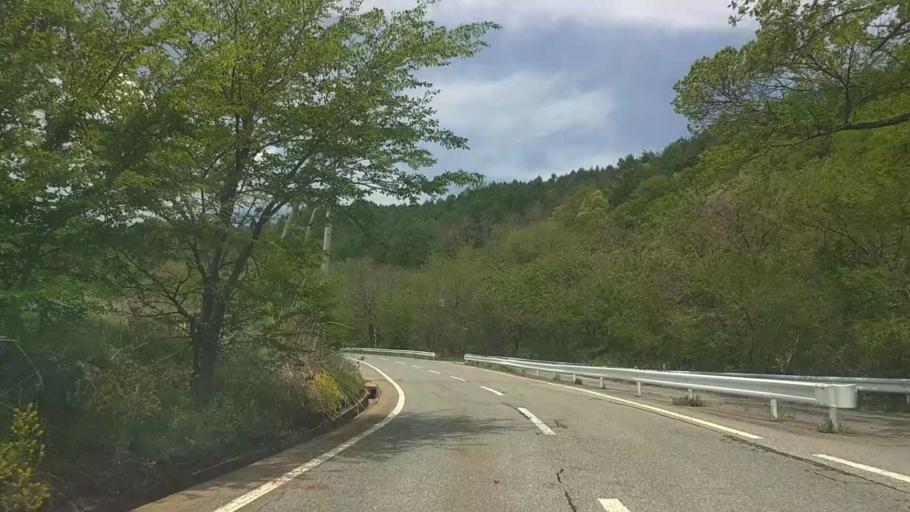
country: JP
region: Nagano
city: Saku
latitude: 36.1055
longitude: 138.4143
